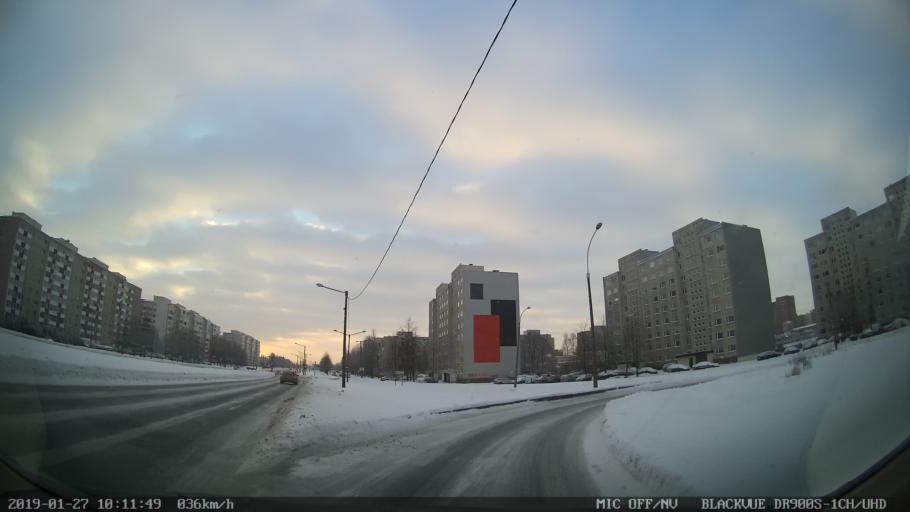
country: EE
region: Harju
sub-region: Tallinna linn
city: Kose
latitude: 59.4390
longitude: 24.8257
